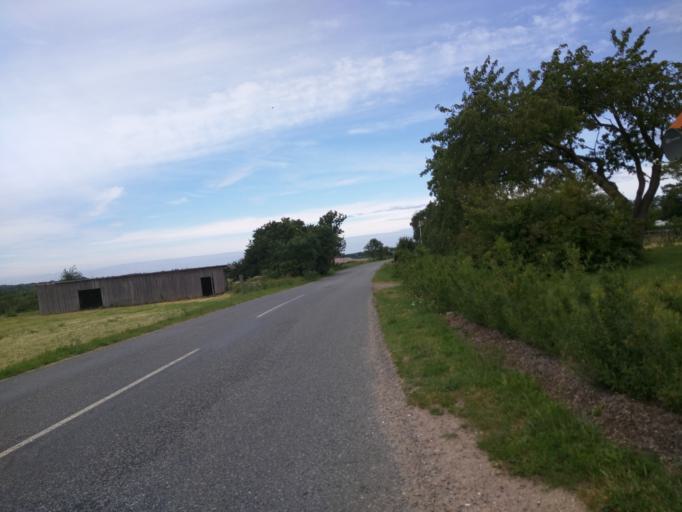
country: DK
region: Zealand
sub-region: Kalundborg Kommune
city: Svebolle
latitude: 55.6765
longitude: 11.3314
